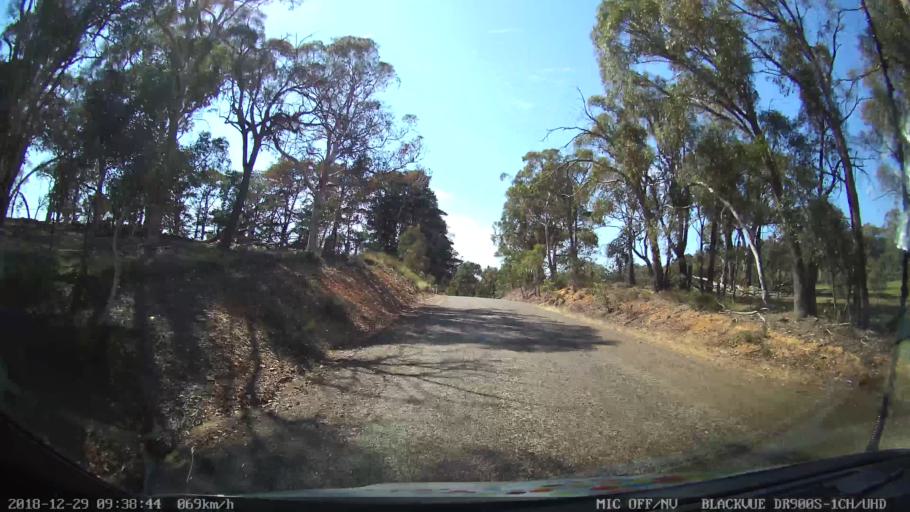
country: AU
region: New South Wales
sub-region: Upper Lachlan Shire
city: Crookwell
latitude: -34.6495
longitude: 149.3780
